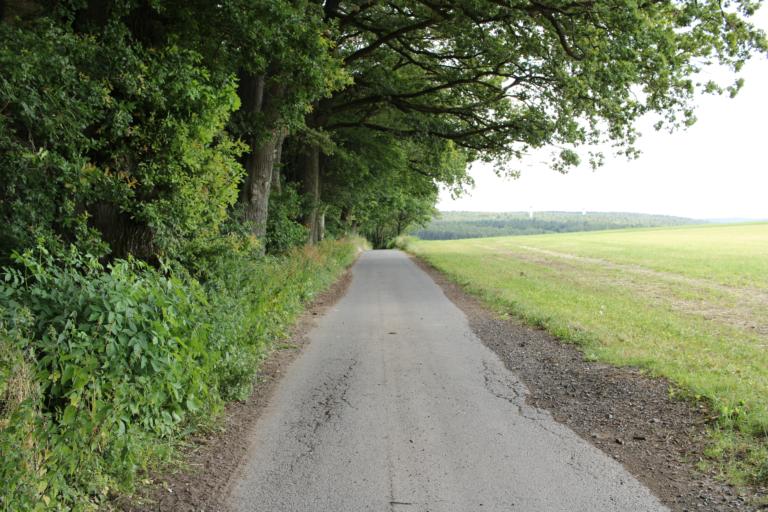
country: DE
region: Hesse
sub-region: Regierungsbezirk Darmstadt
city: Erbach
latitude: 49.6594
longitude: 8.9443
